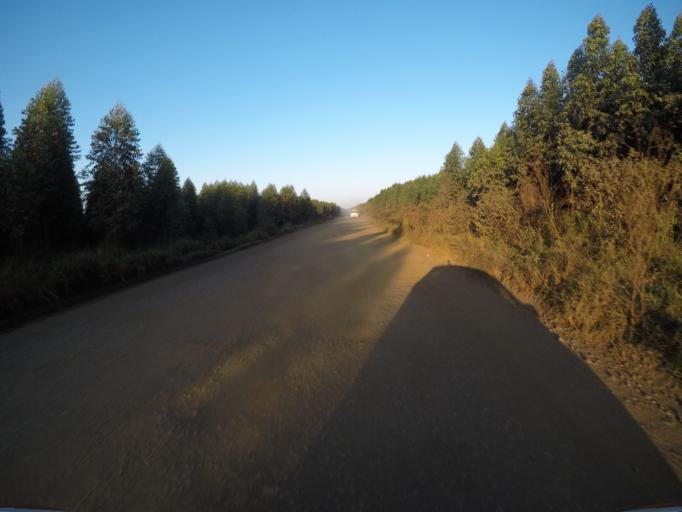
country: ZA
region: KwaZulu-Natal
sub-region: uThungulu District Municipality
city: KwaMbonambi
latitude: -28.6666
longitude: 32.0669
